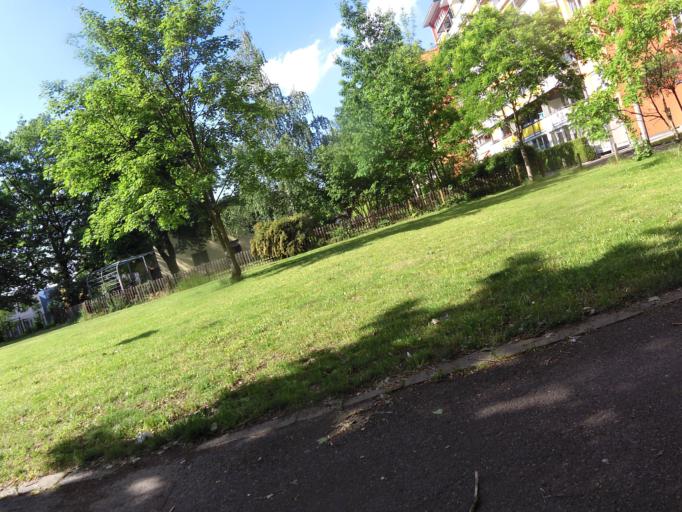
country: DE
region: Saxony
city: Leipzig
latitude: 51.3541
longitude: 12.4189
